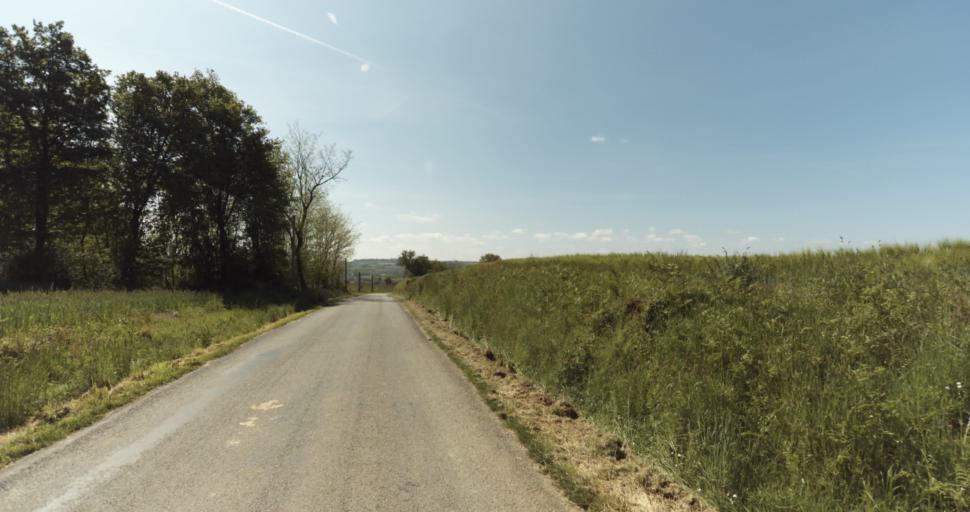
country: FR
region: Limousin
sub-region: Departement de la Haute-Vienne
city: Le Vigen
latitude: 45.7101
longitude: 1.2978
